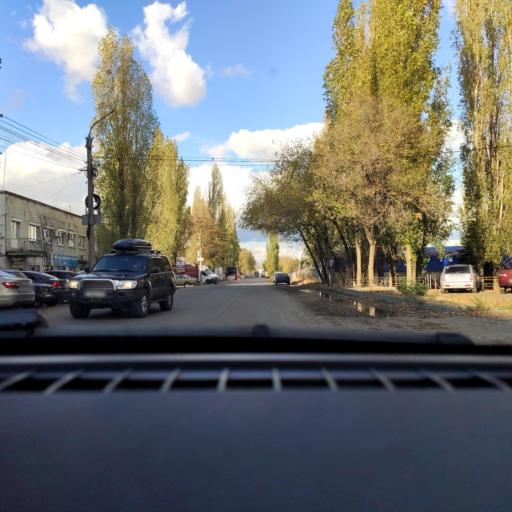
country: RU
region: Voronezj
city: Voronezh
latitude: 51.6503
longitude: 39.2887
